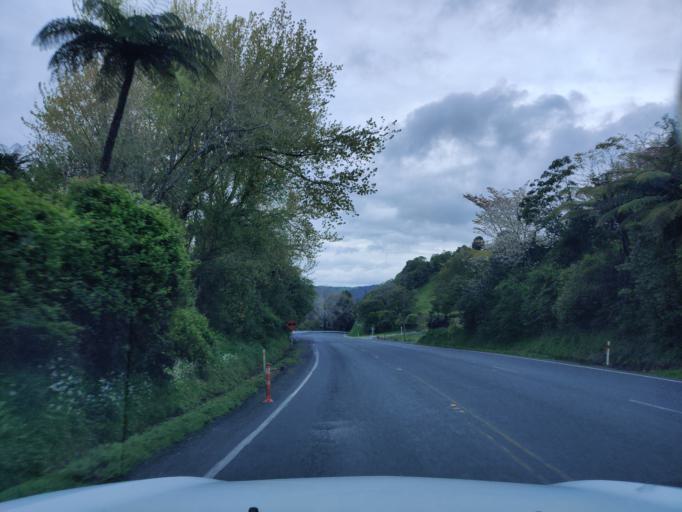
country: NZ
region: Waikato
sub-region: Otorohanga District
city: Otorohanga
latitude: -38.3516
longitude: 175.1608
